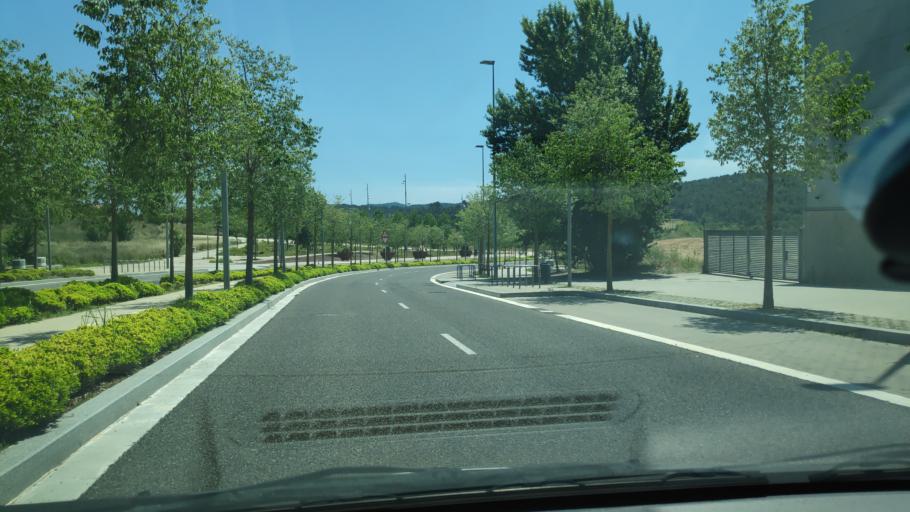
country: ES
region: Catalonia
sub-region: Provincia de Barcelona
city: Cerdanyola del Valles
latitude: 41.4875
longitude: 2.1139
